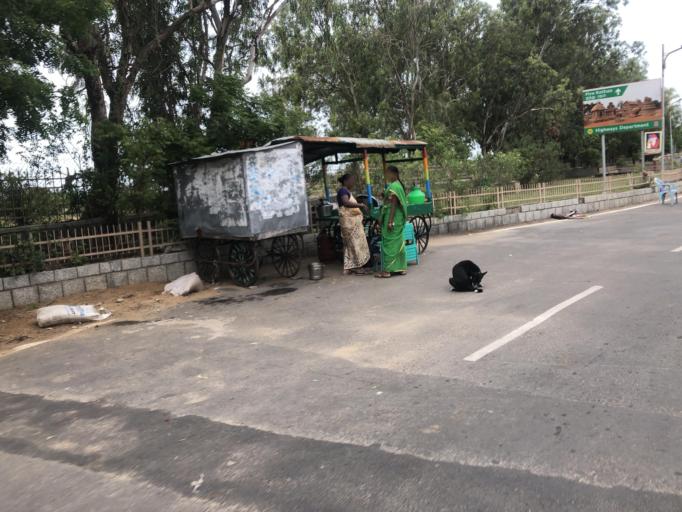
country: IN
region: Tamil Nadu
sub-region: Kancheepuram
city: Mamallapuram
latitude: 12.6117
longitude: 80.1905
